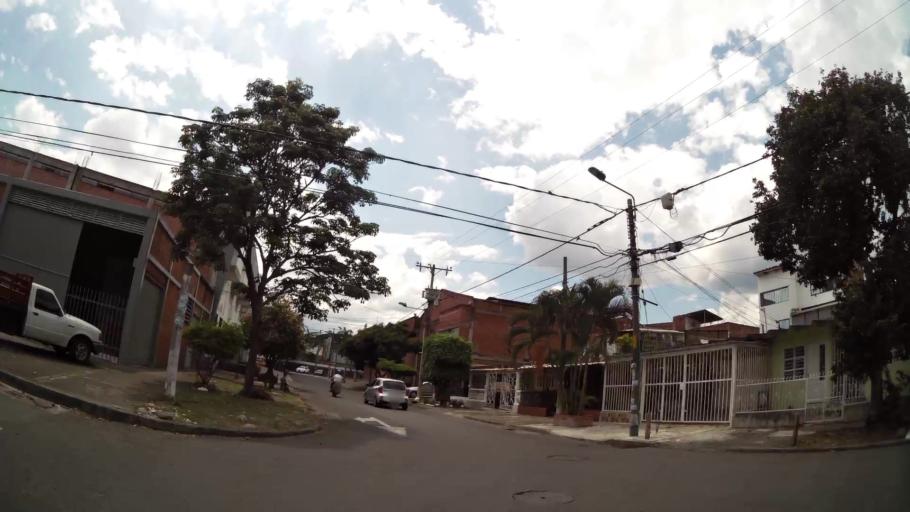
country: CO
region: Valle del Cauca
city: Cali
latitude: 3.4678
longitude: -76.5082
